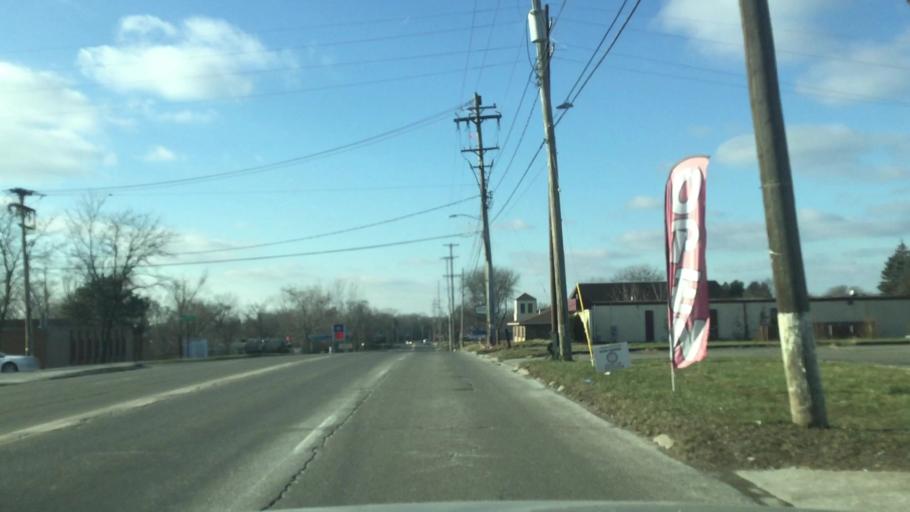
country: US
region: Michigan
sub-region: Genesee County
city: Flint
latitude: 43.0259
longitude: -83.7366
